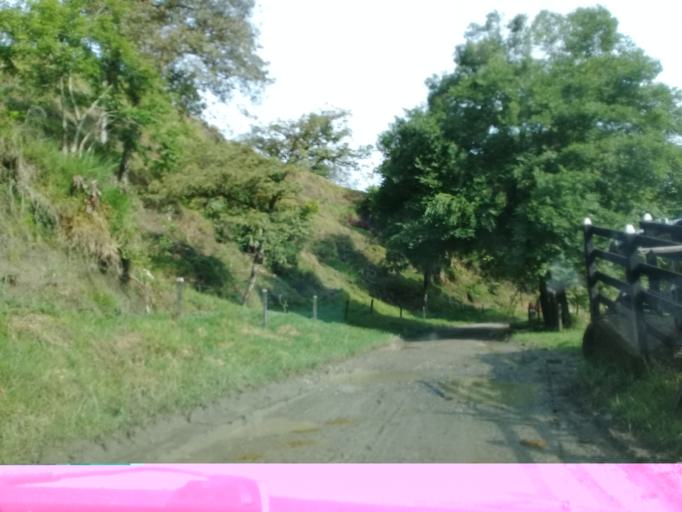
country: CO
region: Antioquia
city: Puerto Triunfo
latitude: 5.7205
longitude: -74.4674
